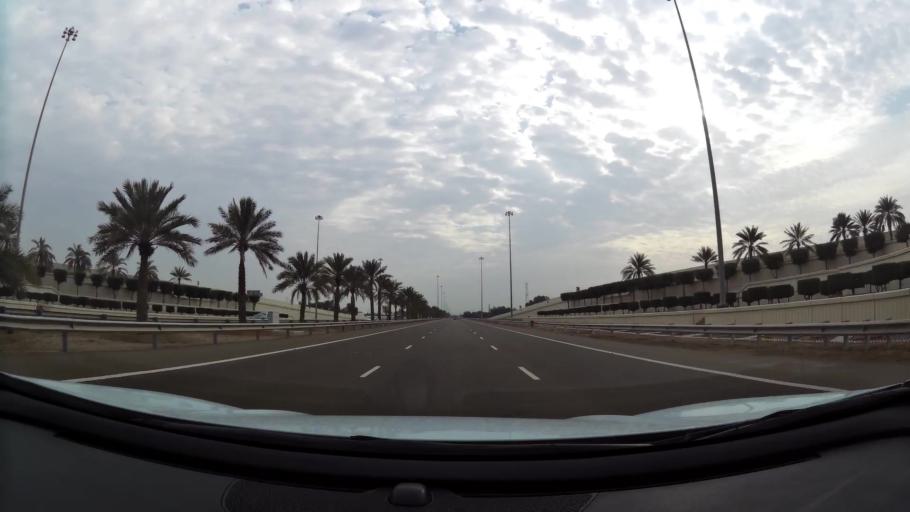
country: AE
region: Abu Dhabi
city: Al Ain
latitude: 24.1700
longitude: 55.1018
